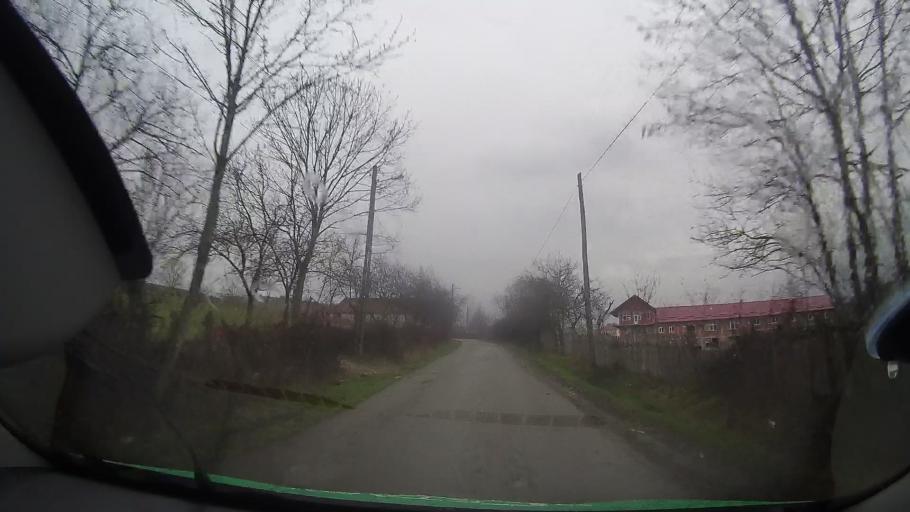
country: RO
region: Bihor
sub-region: Comuna Uileacu de Beius
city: Uileacu de Beius
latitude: 46.7056
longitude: 22.2232
